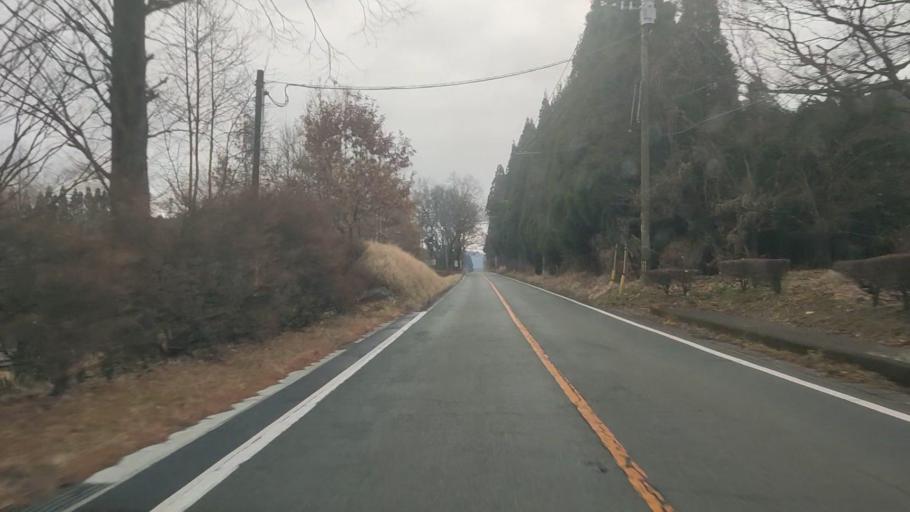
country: JP
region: Kumamoto
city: Aso
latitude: 32.8498
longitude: 131.1500
